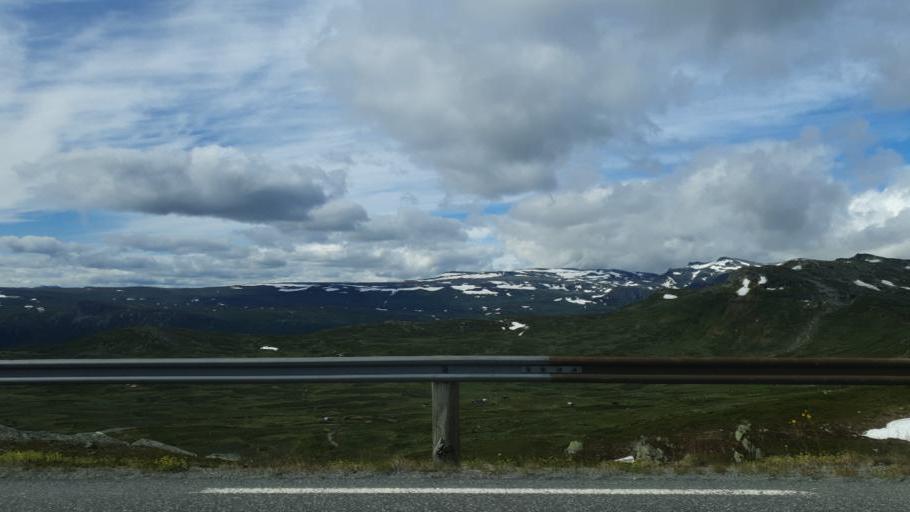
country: NO
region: Oppland
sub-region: Vestre Slidre
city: Slidre
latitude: 61.2863
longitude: 8.8159
